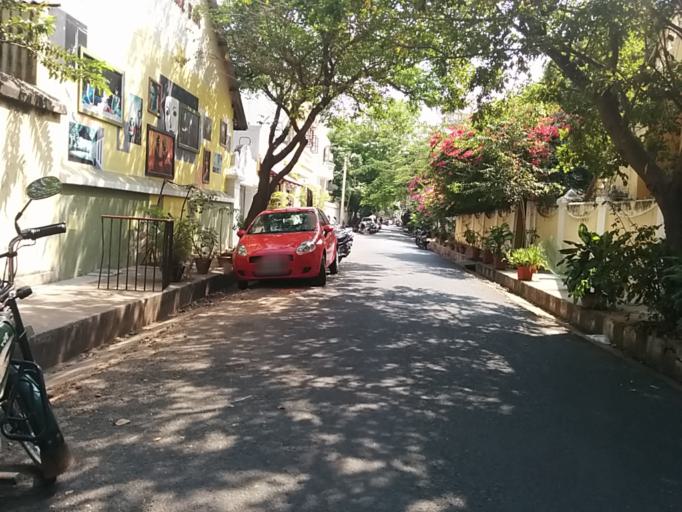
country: IN
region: Pondicherry
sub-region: Puducherry
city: Puducherry
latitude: 11.9297
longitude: 79.8340
